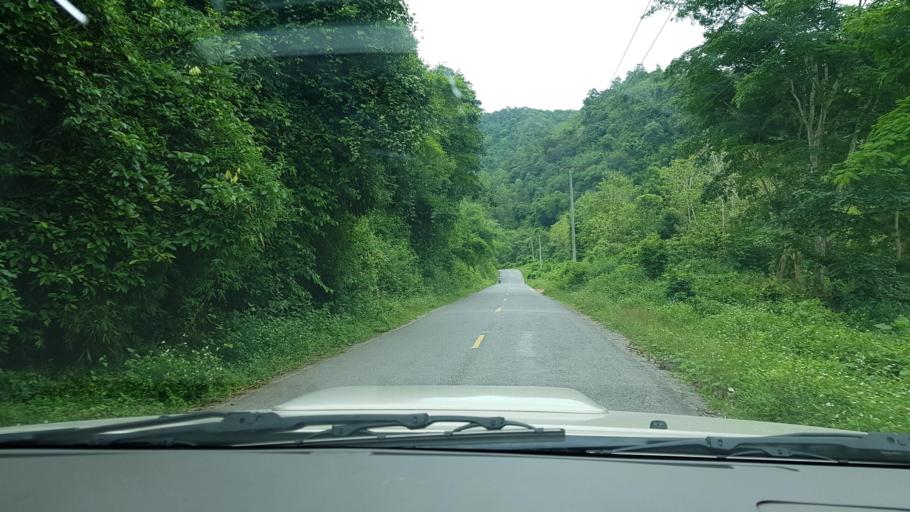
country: LA
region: Oudomxai
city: Muang La
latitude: 20.8665
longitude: 102.1279
